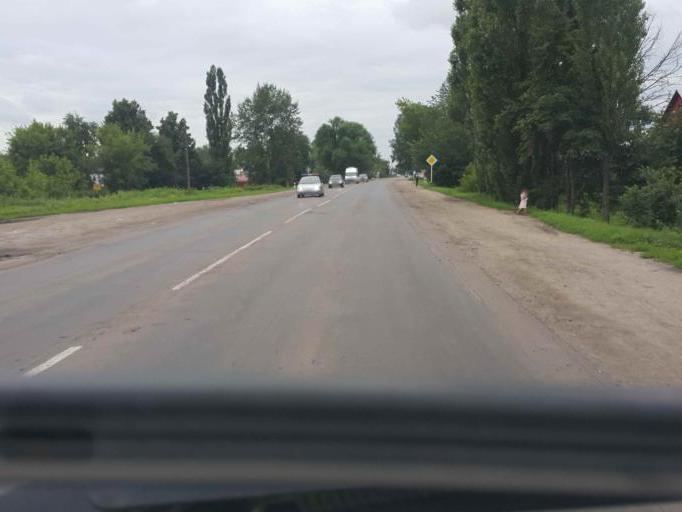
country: RU
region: Tambov
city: Zavoronezhskoye
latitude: 52.8845
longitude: 40.5517
